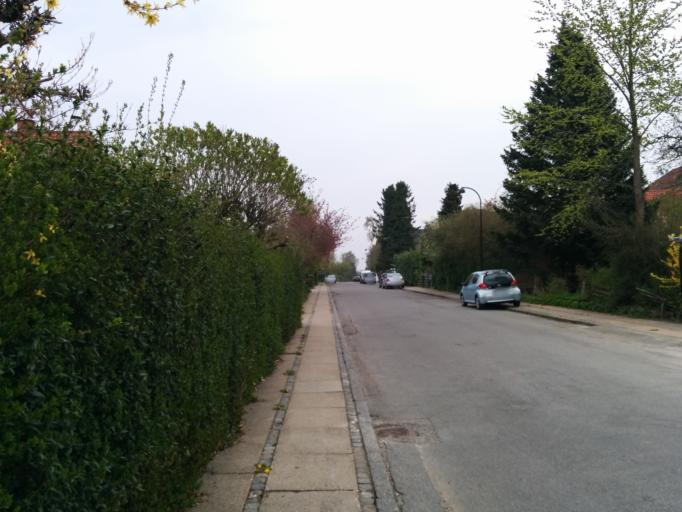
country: DK
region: Capital Region
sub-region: Gladsaxe Municipality
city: Buddinge
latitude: 55.7312
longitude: 12.5225
